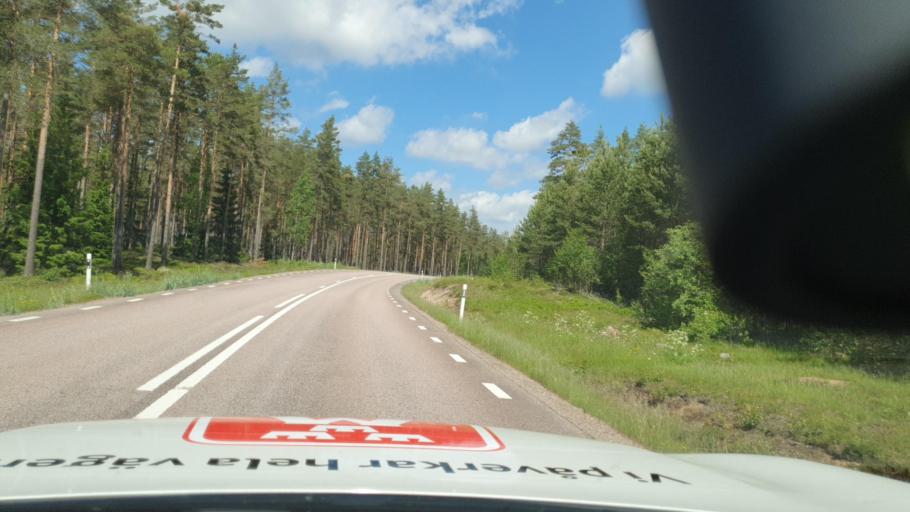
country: SE
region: Vaermland
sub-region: Filipstads Kommun
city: Filipstad
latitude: 59.6312
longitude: 13.9536
